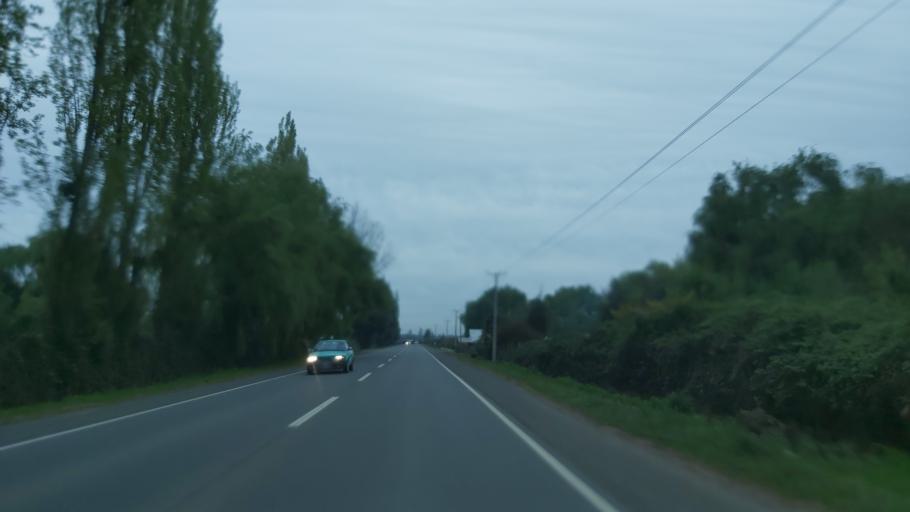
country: CL
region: Maule
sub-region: Provincia de Linares
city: Linares
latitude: -35.7632
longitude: -71.5100
